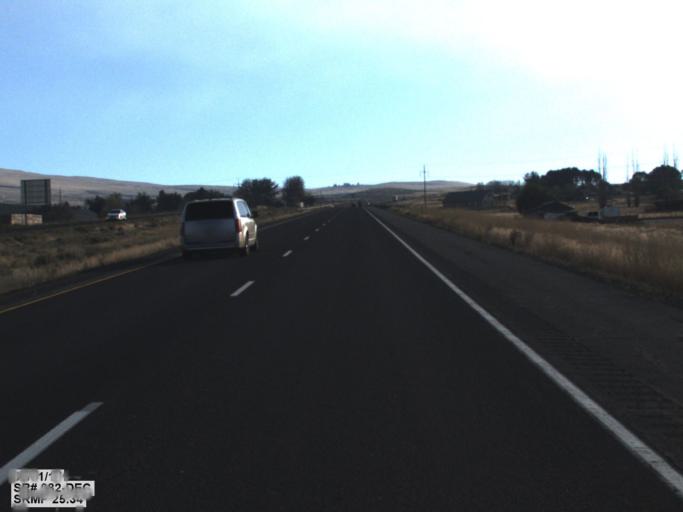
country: US
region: Washington
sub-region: Yakima County
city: Selah
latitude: 46.6885
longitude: -120.4605
